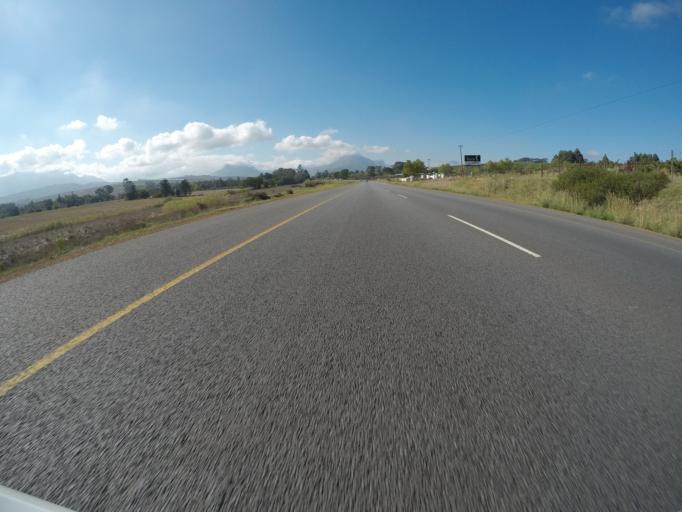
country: ZA
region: Western Cape
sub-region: Cape Winelands District Municipality
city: Stellenbosch
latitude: -33.8878
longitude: 18.8233
